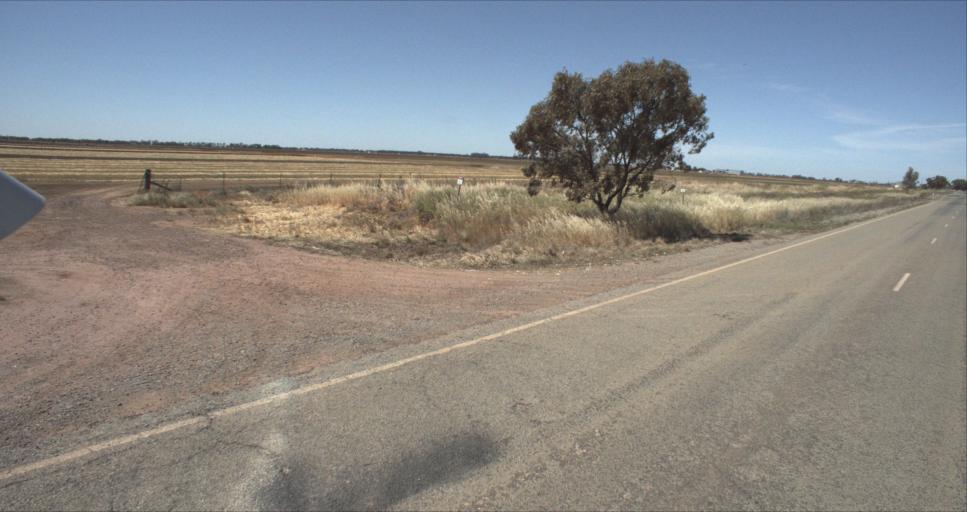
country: AU
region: New South Wales
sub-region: Leeton
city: Leeton
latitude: -34.4955
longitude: 146.2879
